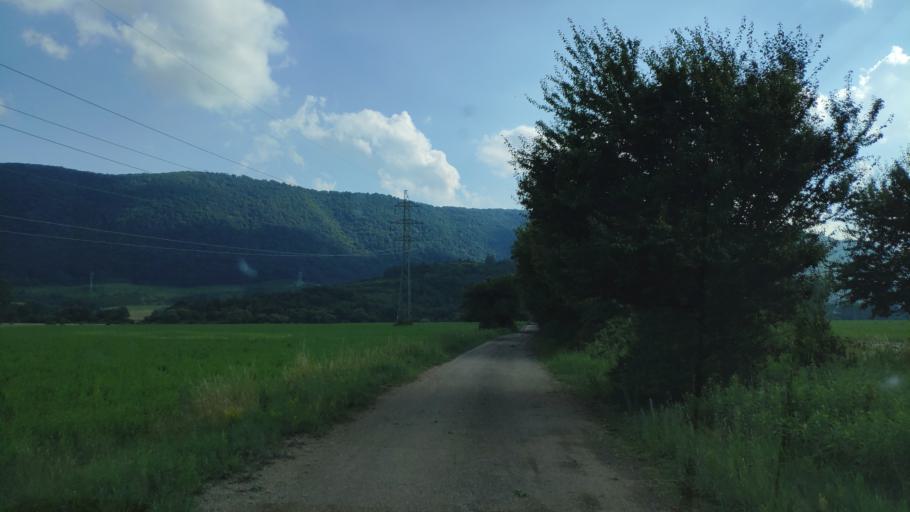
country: SK
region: Kosicky
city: Medzev
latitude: 48.5947
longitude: 20.7310
